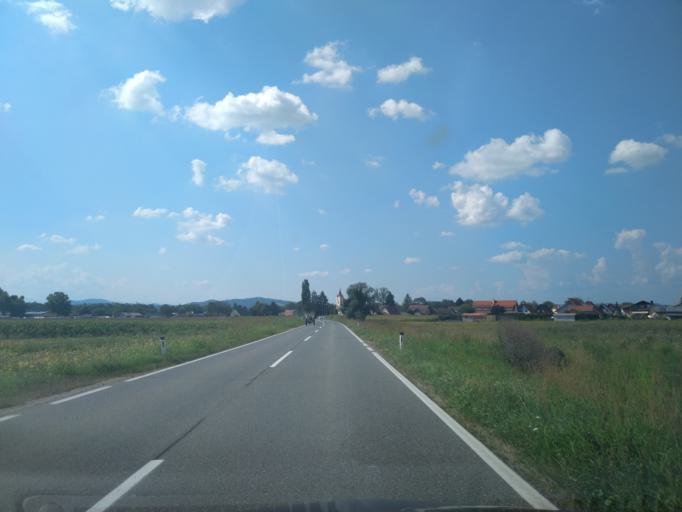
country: AT
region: Styria
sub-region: Politischer Bezirk Leibnitz
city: Gabersdorf
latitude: 46.7620
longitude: 15.5865
